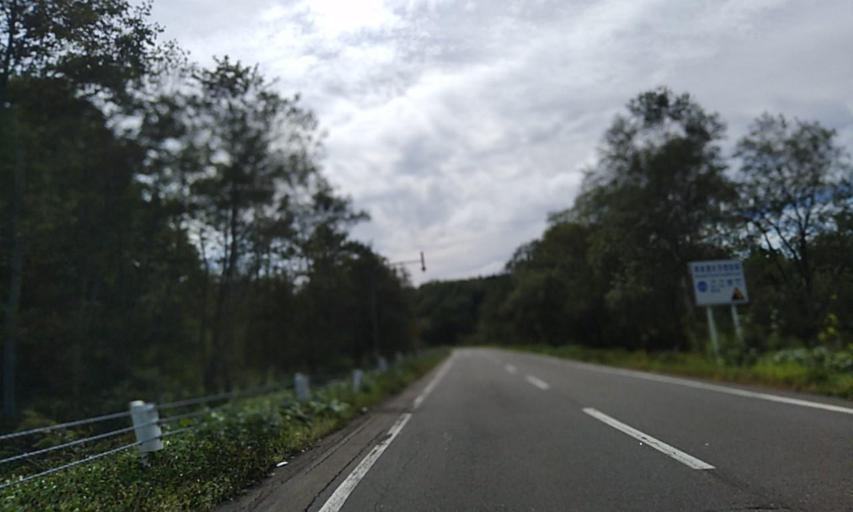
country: JP
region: Hokkaido
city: Kushiro
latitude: 42.8421
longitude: 143.8412
